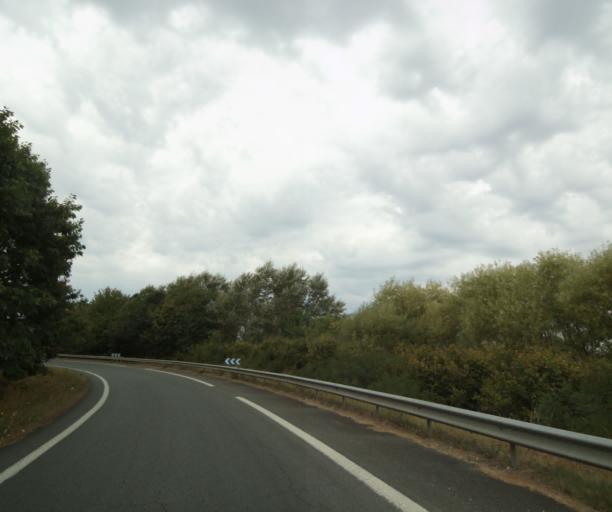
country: FR
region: Poitou-Charentes
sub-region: Departement de la Charente-Maritime
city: Tonnay-Charente
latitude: 45.9576
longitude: -0.8854
